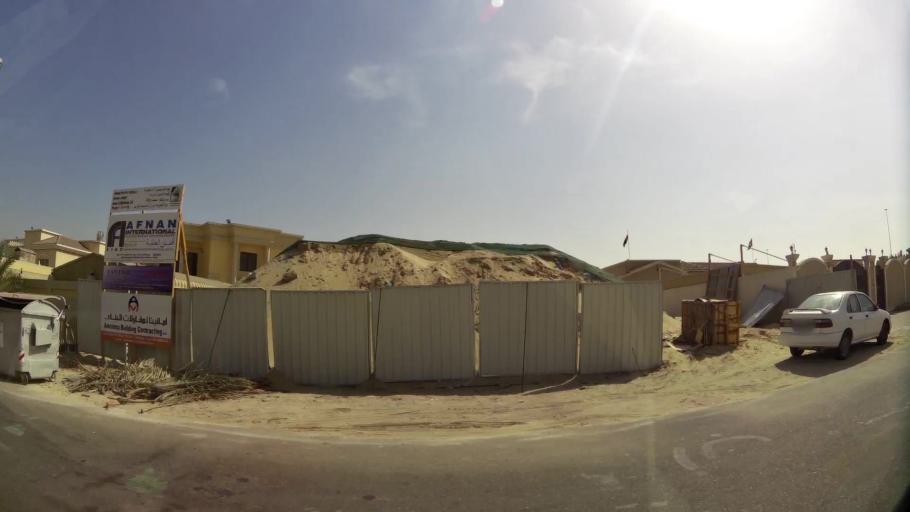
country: AE
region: Ash Shariqah
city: Sharjah
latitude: 25.2679
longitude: 55.4112
